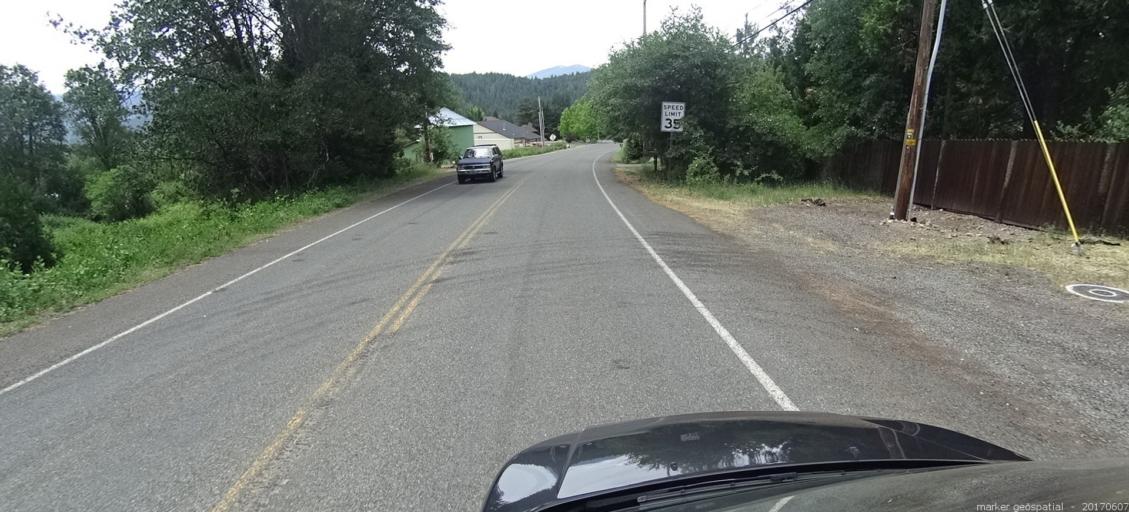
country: US
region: California
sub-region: Siskiyou County
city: Mount Shasta
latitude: 41.2983
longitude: -122.3154
